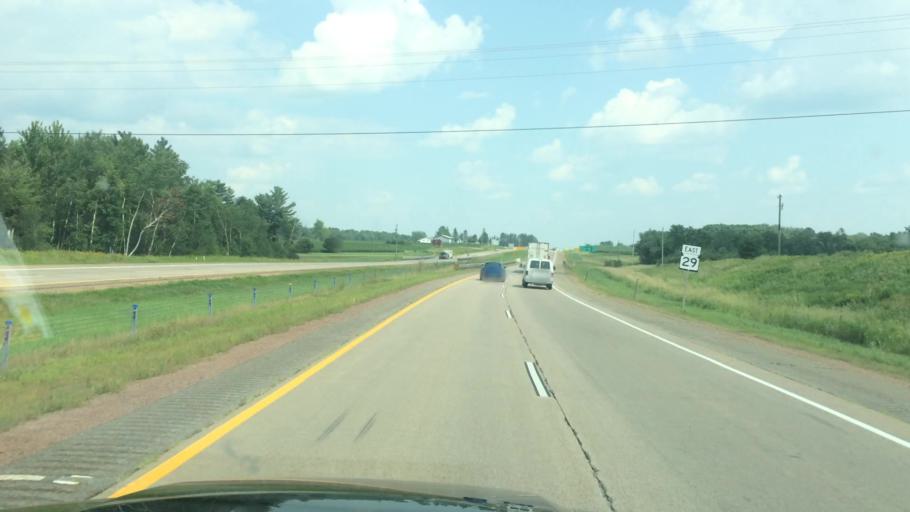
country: US
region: Wisconsin
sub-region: Clark County
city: Abbotsford
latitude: 44.9456
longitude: -90.2800
